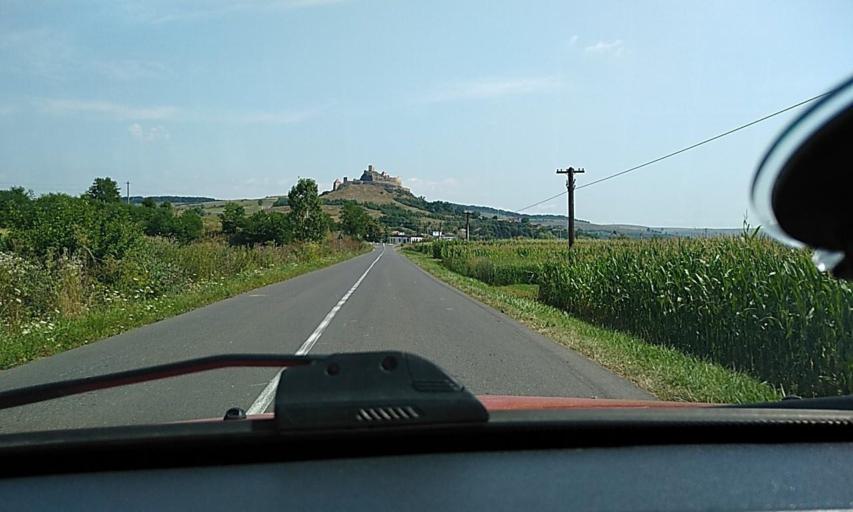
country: RO
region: Brasov
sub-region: Oras Rupea
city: Rupea
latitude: 46.0283
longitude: 25.2029
